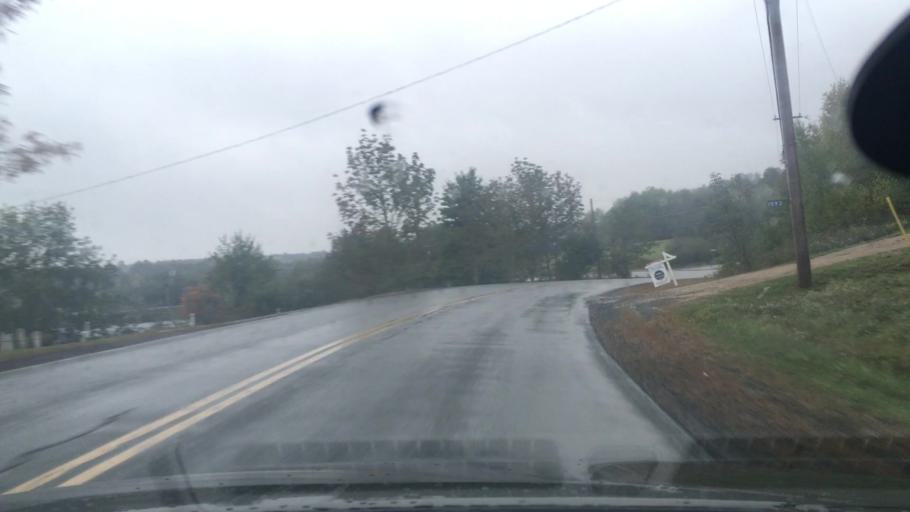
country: CA
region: Nova Scotia
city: Windsor
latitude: 44.8400
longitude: -64.2363
